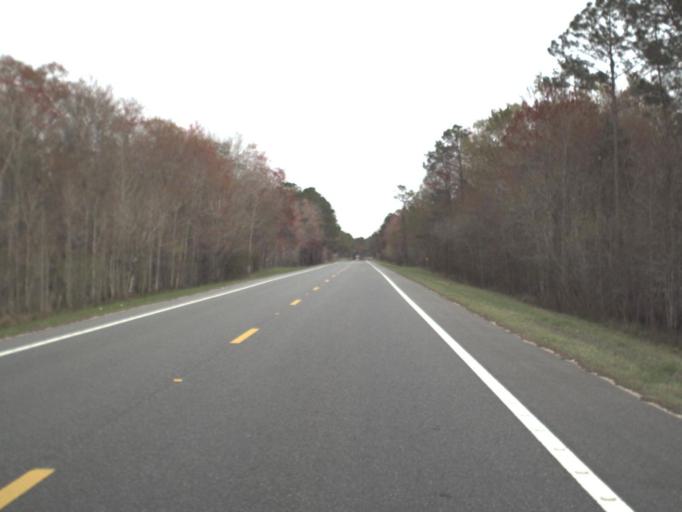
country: US
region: Florida
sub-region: Leon County
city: Woodville
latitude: 30.1883
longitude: -84.0344
